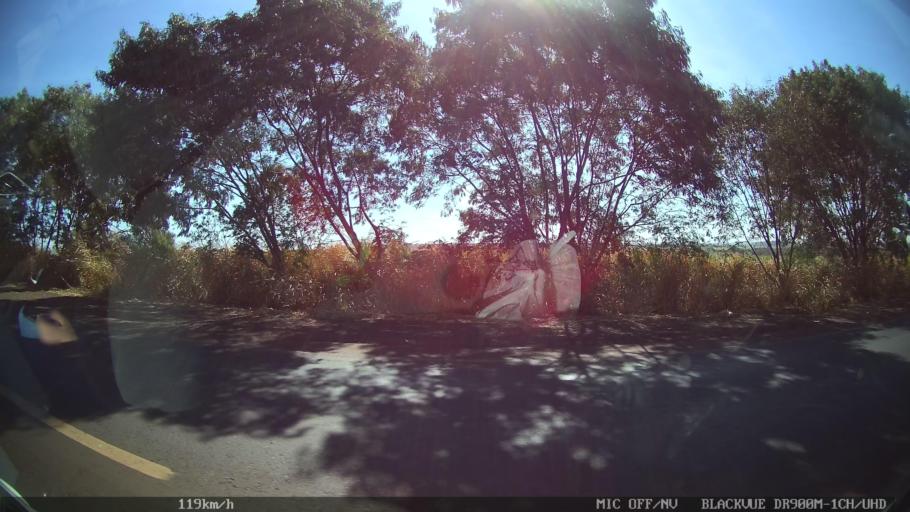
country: BR
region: Sao Paulo
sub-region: Barretos
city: Barretos
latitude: -20.4887
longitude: -48.5186
